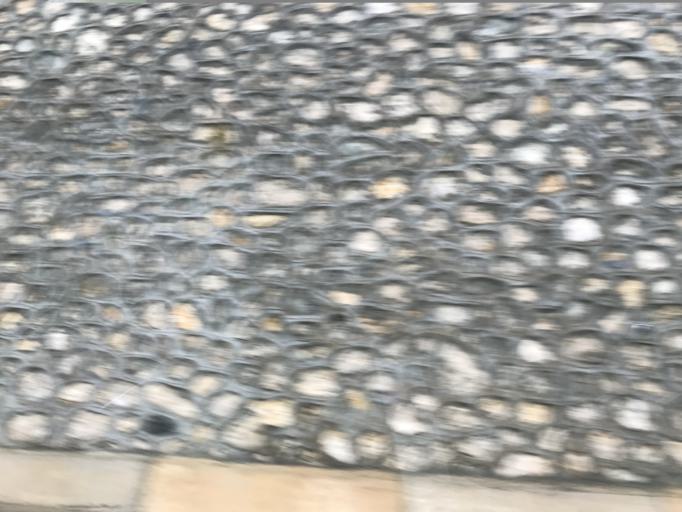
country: TR
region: Bartin
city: Amasra
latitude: 41.7338
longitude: 32.3785
